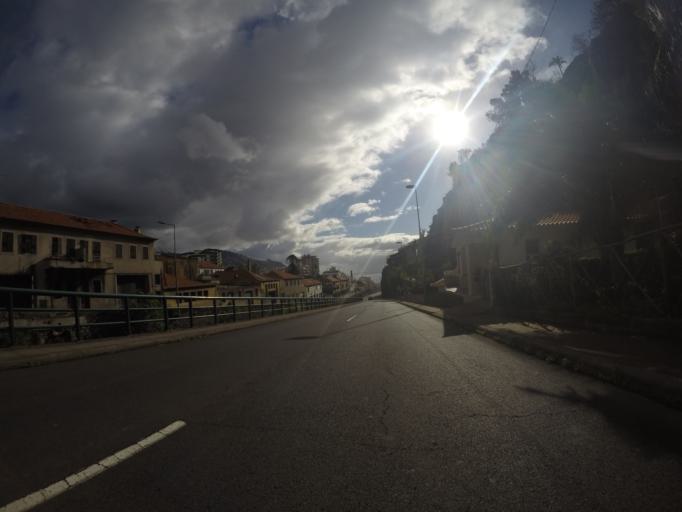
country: PT
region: Madeira
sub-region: Funchal
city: Nossa Senhora do Monte
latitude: 32.6564
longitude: -16.9173
